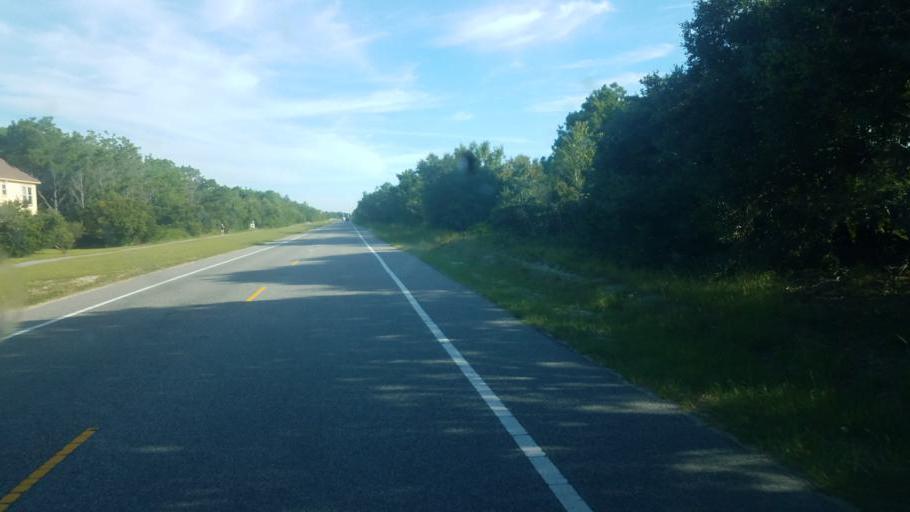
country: US
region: North Carolina
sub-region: Dare County
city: Southern Shores
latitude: 36.3353
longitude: -75.8176
